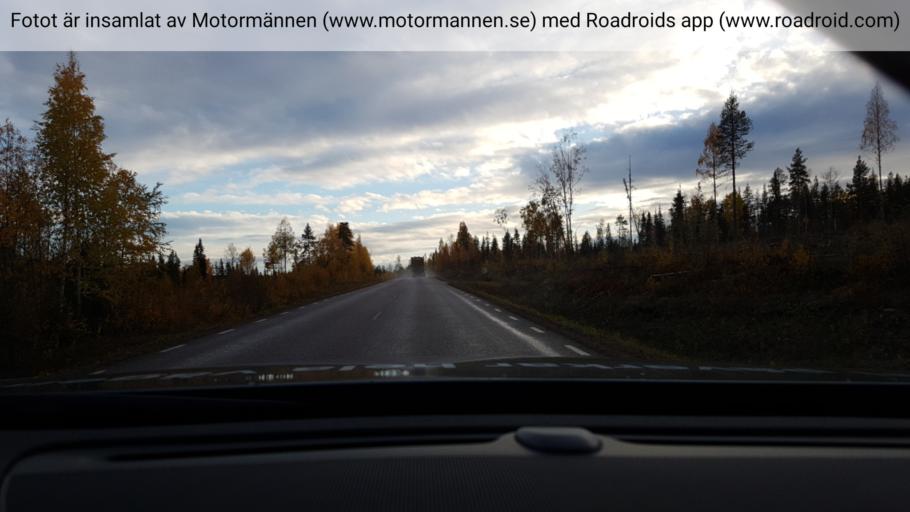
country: SE
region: Norrbotten
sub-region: Overkalix Kommun
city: OEverkalix
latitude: 66.8165
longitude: 22.7444
